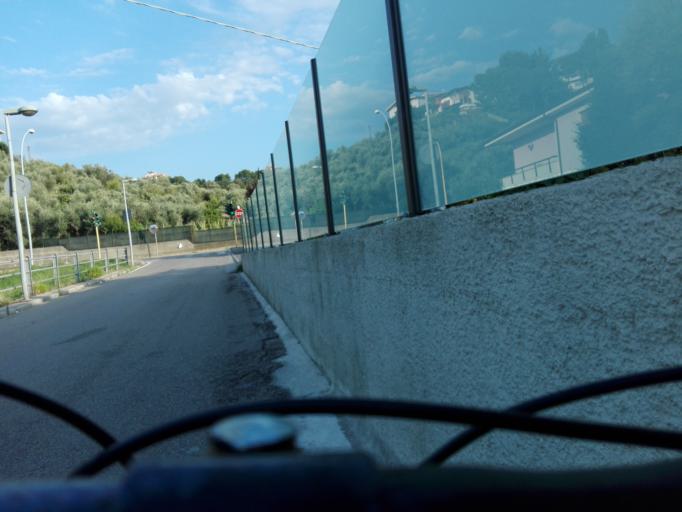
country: IT
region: Abruzzo
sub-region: Provincia di Pescara
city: Montesilvano Marina
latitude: 42.5063
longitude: 14.1438
